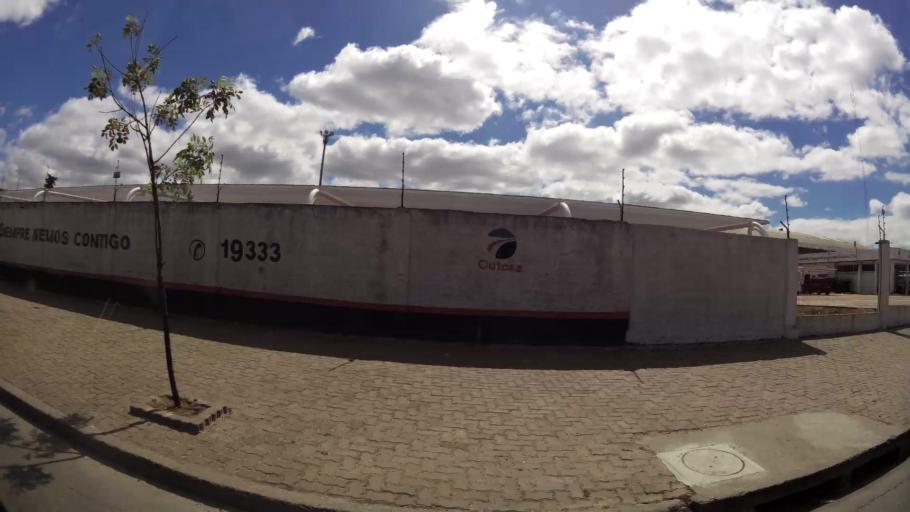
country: UY
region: Canelones
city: Paso de Carrasco
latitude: -34.8639
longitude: -56.1222
